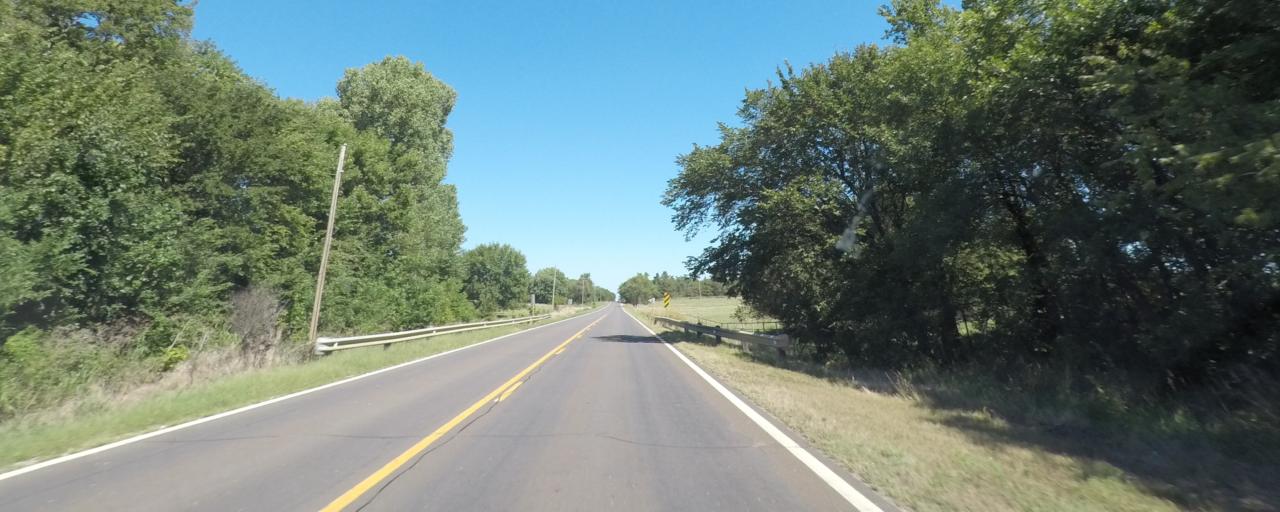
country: US
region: Kansas
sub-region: Sumner County
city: Wellington
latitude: 37.0675
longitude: -97.4013
